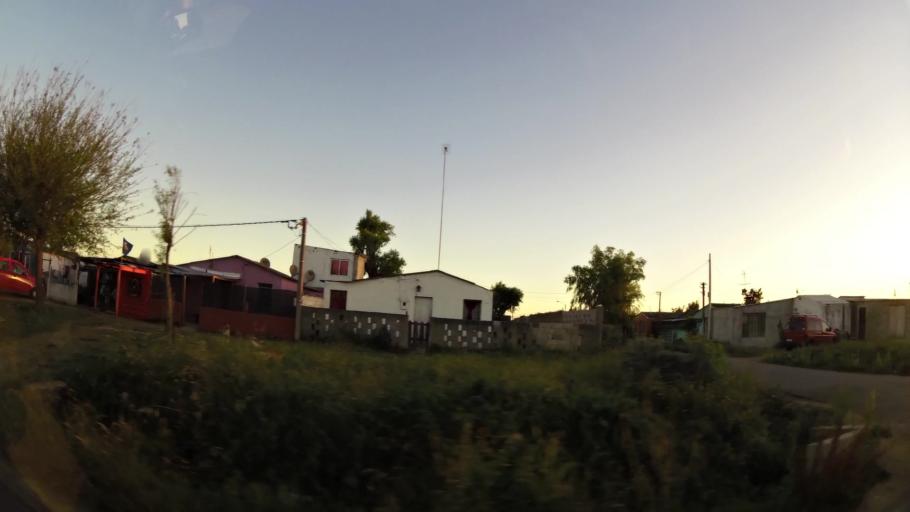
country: UY
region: Montevideo
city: Montevideo
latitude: -34.8304
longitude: -56.1651
